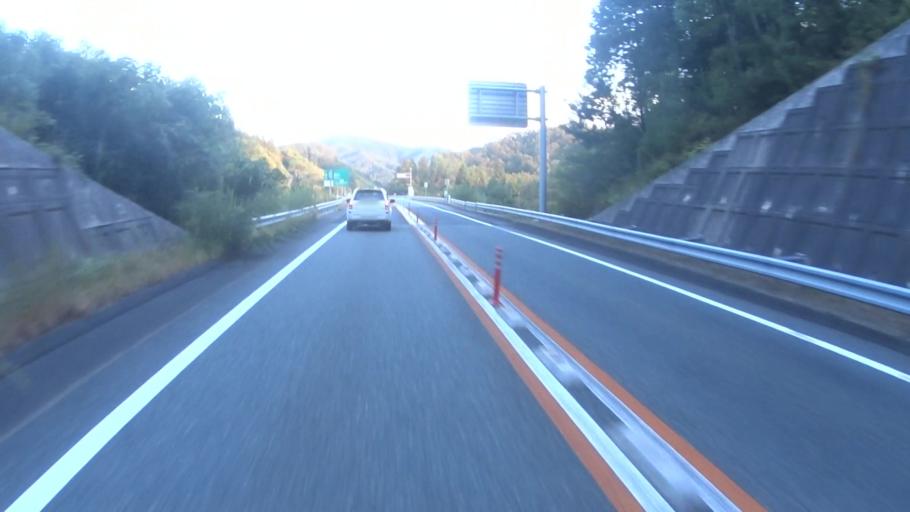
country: JP
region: Kyoto
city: Ayabe
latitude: 35.3449
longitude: 135.2983
